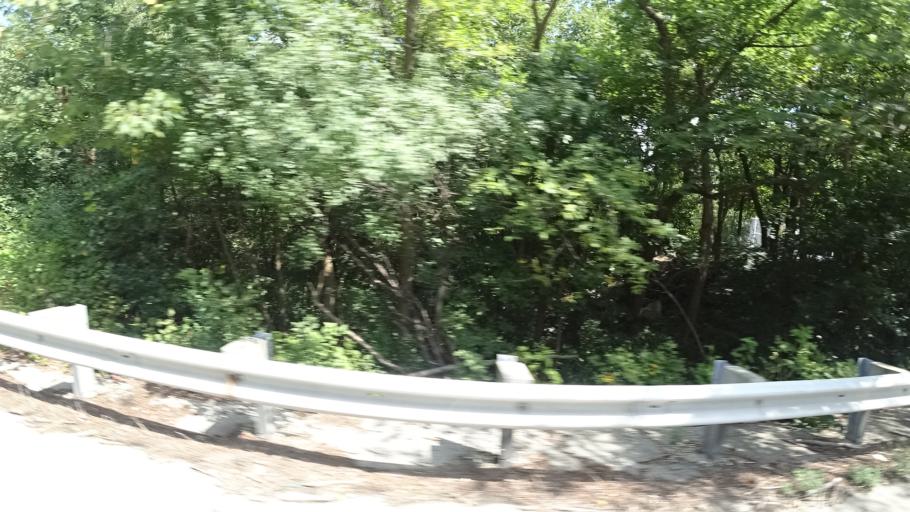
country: US
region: Illinois
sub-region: Cook County
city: Orland Park
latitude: 41.6232
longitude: -87.8193
